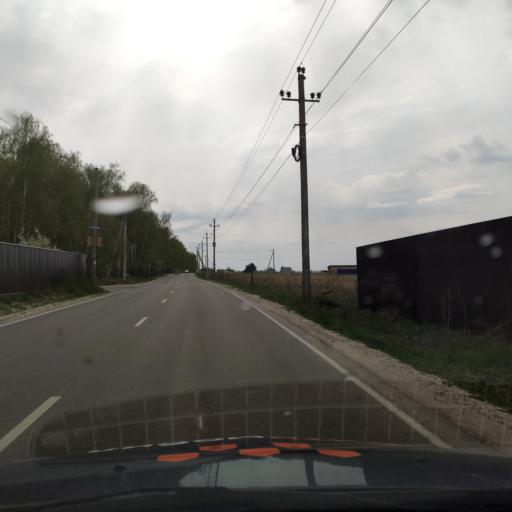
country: RU
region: Voronezj
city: Podgornoye
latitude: 51.8448
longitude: 39.1458
